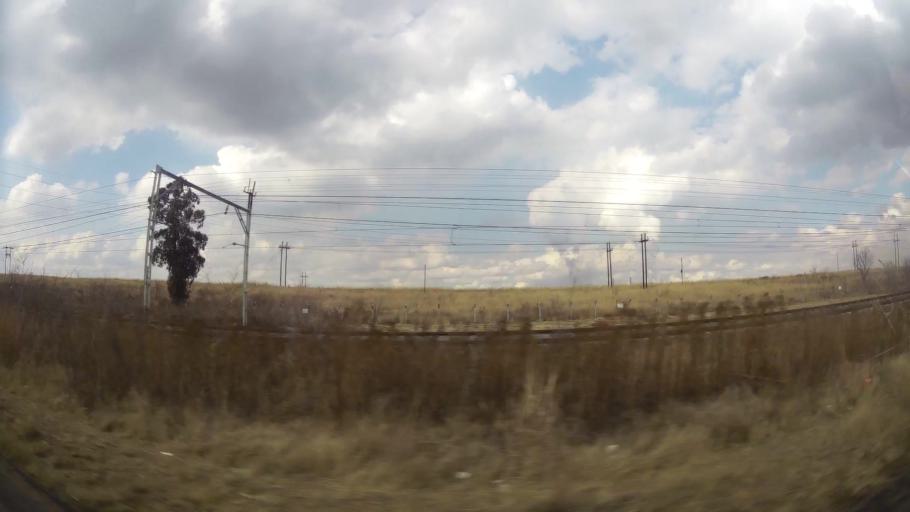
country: ZA
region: Gauteng
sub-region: Sedibeng District Municipality
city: Vereeniging
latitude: -26.7050
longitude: 27.9324
